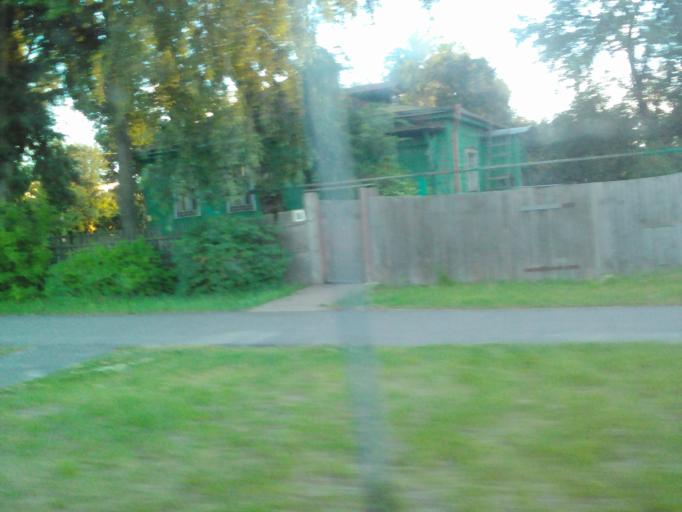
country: RU
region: Kursk
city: Kursk
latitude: 51.7279
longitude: 36.1589
